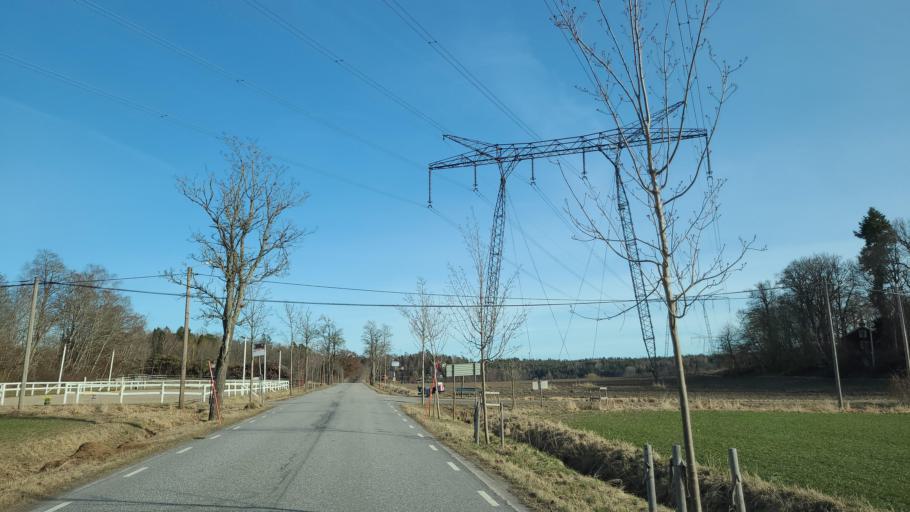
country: SE
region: Stockholm
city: Stenhamra
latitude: 59.2821
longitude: 17.6666
